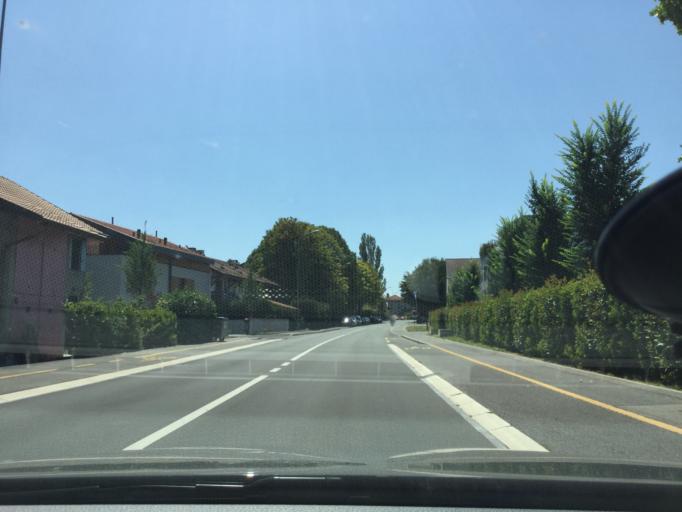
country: CH
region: Geneva
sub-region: Geneva
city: Corsier
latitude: 46.2556
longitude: 6.2064
